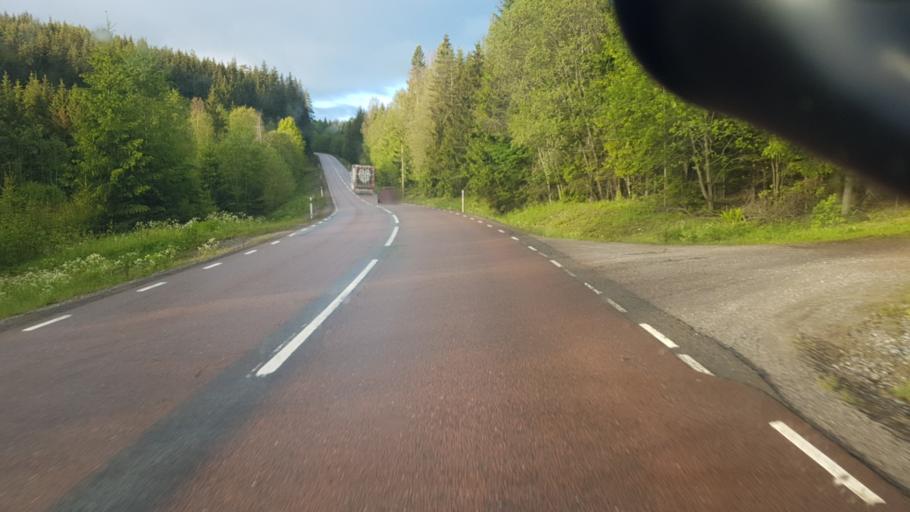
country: SE
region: Vaermland
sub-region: Eda Kommun
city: Amotfors
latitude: 59.8121
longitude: 12.3196
